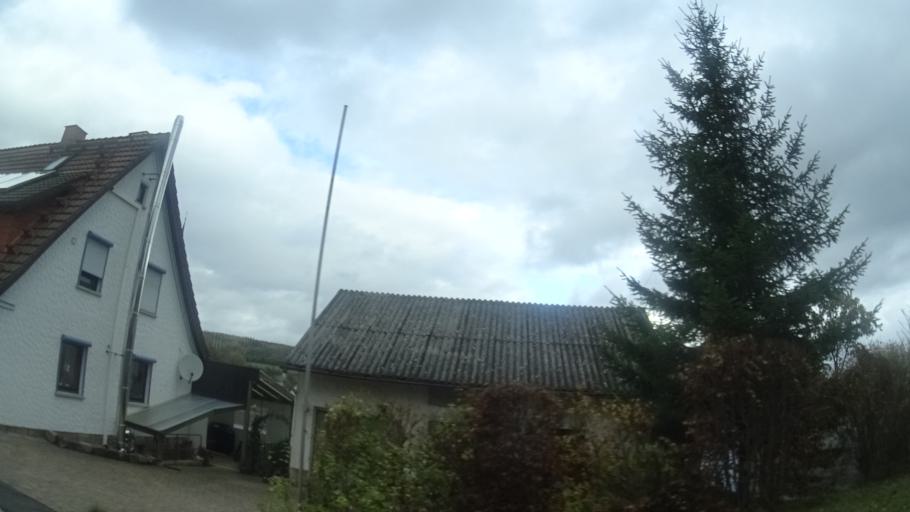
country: DE
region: Bavaria
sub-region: Regierungsbezirk Unterfranken
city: Oberelsbach
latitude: 50.3781
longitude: 10.1033
